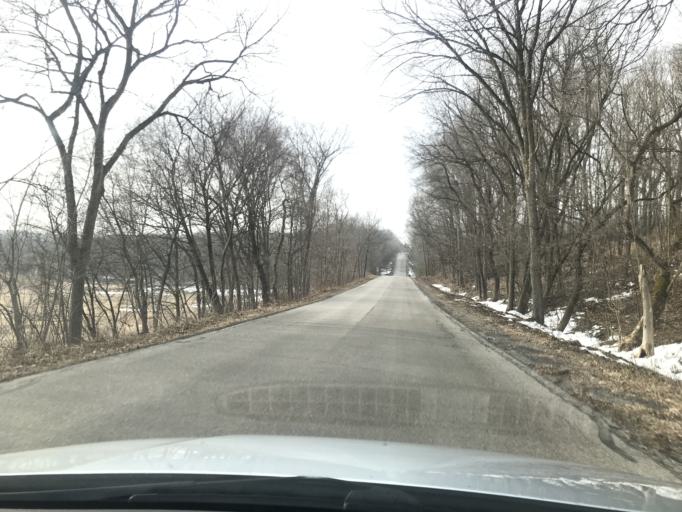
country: US
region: Wisconsin
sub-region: Oconto County
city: Oconto Falls
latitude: 44.8675
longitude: -88.1466
